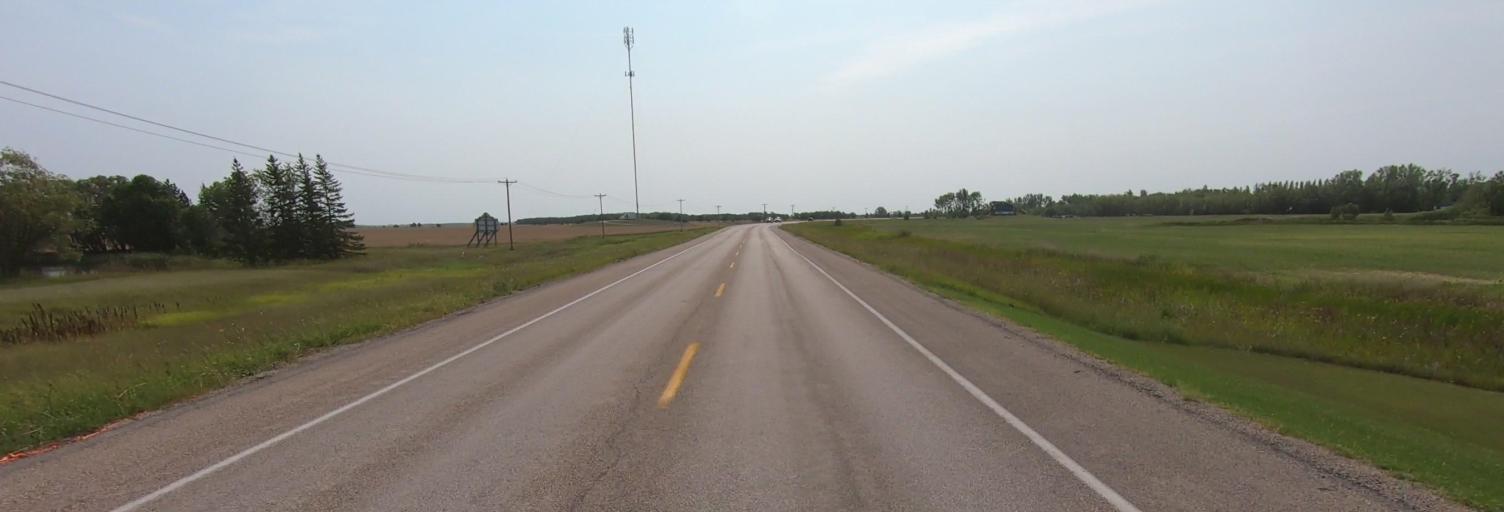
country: CA
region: Manitoba
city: Niverville
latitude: 49.6630
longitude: -97.1062
